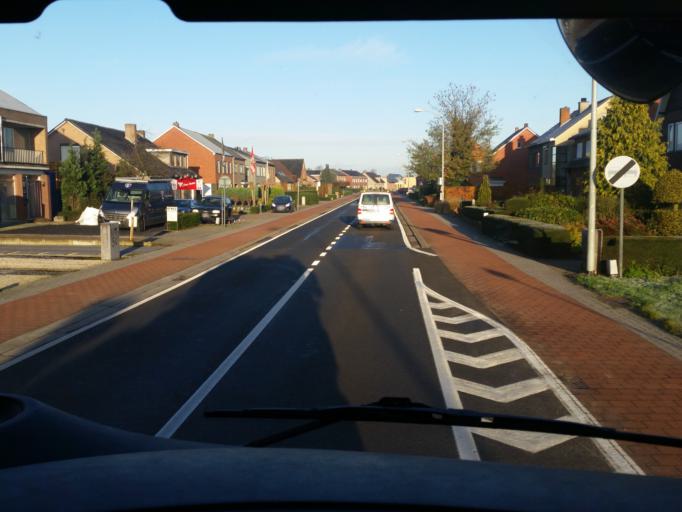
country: BE
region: Flanders
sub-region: Provincie Antwerpen
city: Arendonk
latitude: 51.3126
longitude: 5.0918
